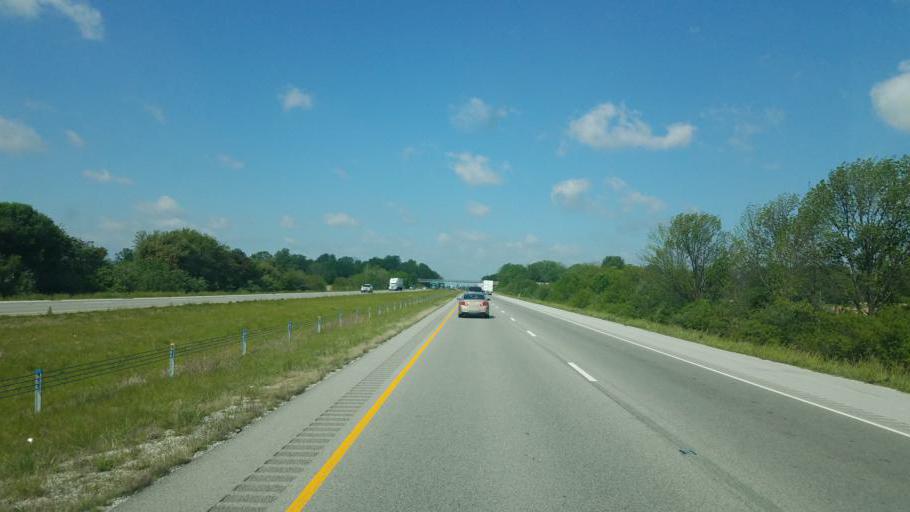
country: US
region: Indiana
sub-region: Morgan County
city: Monrovia
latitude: 39.5886
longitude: -86.5629
